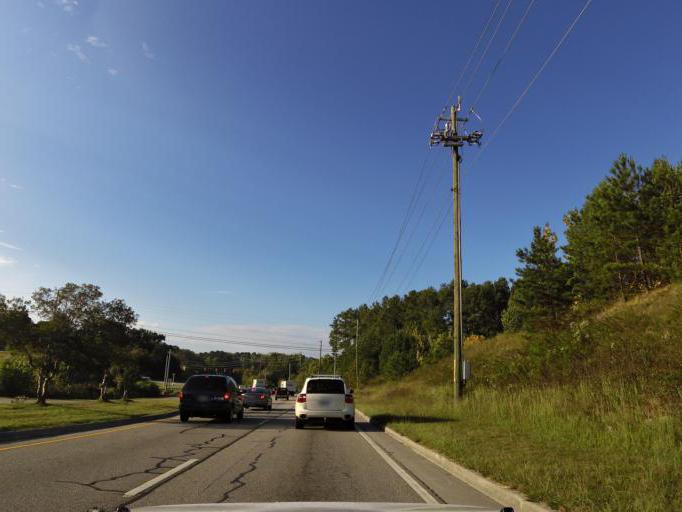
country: US
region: Georgia
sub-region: Cobb County
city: Powder Springs
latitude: 33.9017
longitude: -84.6280
